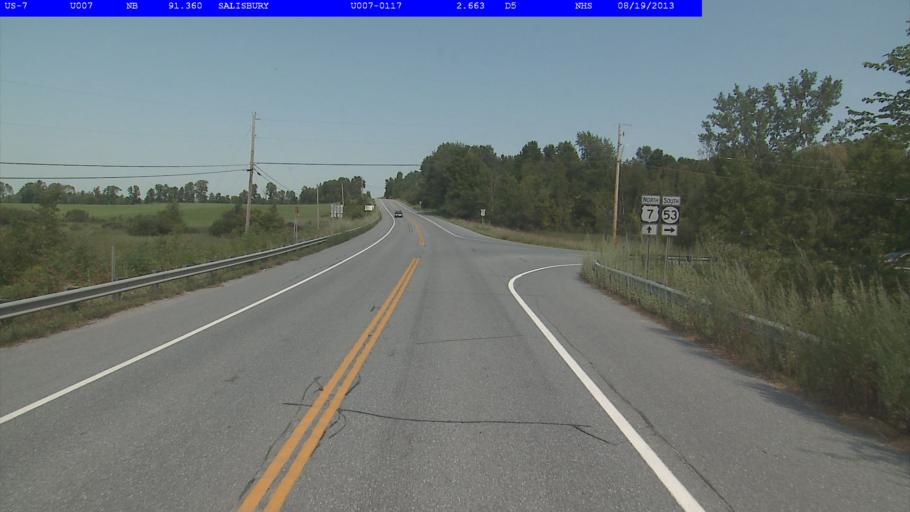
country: US
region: Vermont
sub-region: Addison County
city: Middlebury (village)
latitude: 43.9301
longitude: -73.1089
